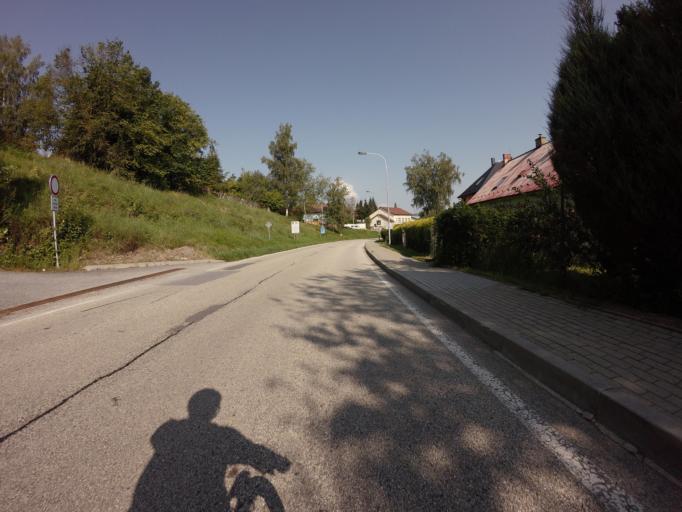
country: CZ
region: Jihocesky
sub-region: Okres Cesky Krumlov
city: Vyssi Brod
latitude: 48.6110
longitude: 14.3119
